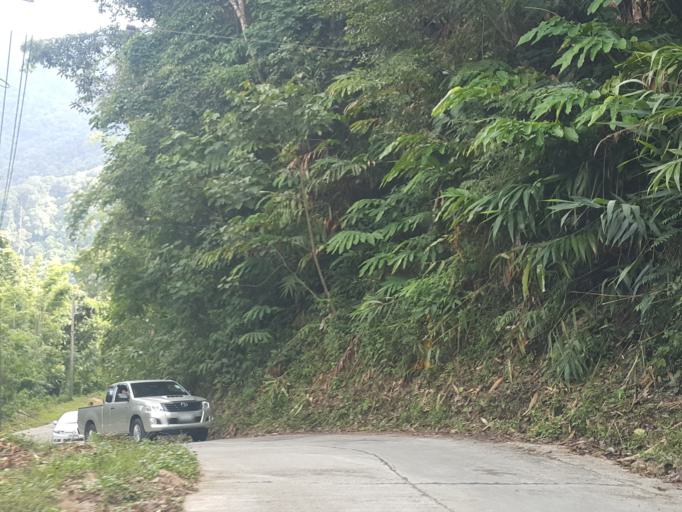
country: TH
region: Chiang Mai
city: Mae On
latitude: 18.8883
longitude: 99.3573
